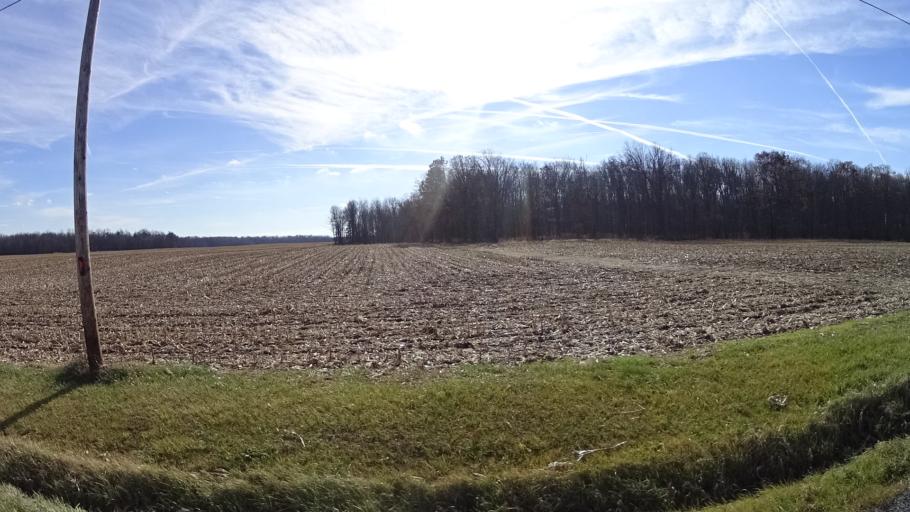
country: US
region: Ohio
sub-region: Huron County
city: New London
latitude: 41.1034
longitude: -82.3240
